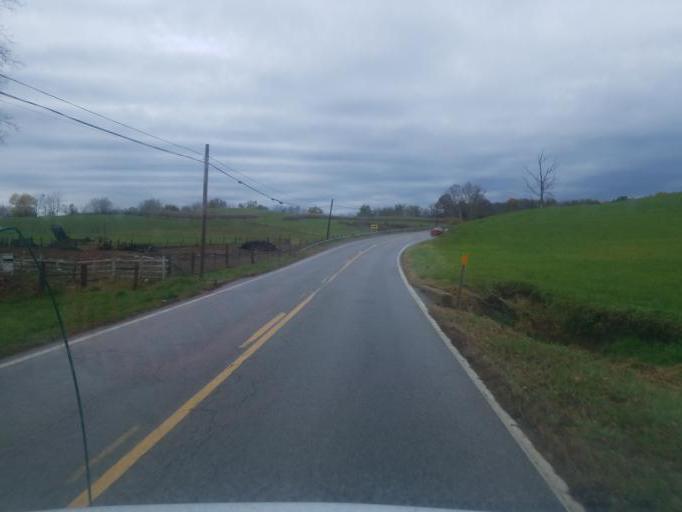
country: US
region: Ohio
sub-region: Morgan County
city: McConnelsville
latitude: 39.5062
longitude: -81.8563
